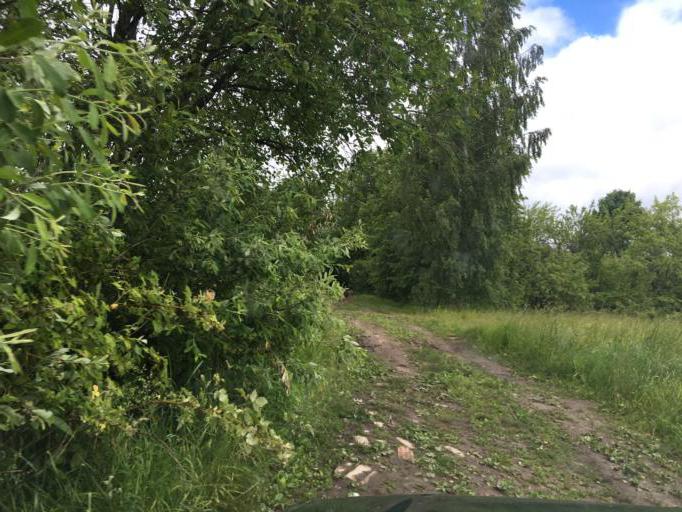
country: LV
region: Balvu Rajons
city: Balvi
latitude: 57.2145
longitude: 27.3118
